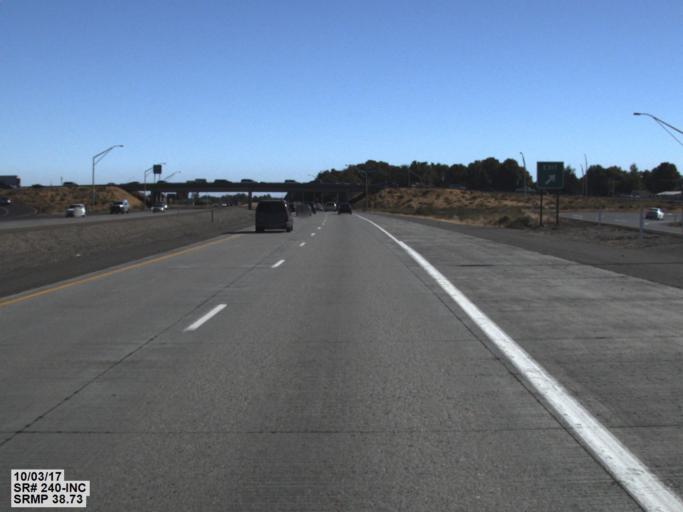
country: US
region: Washington
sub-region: Franklin County
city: West Pasco
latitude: 46.2327
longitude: -119.2270
